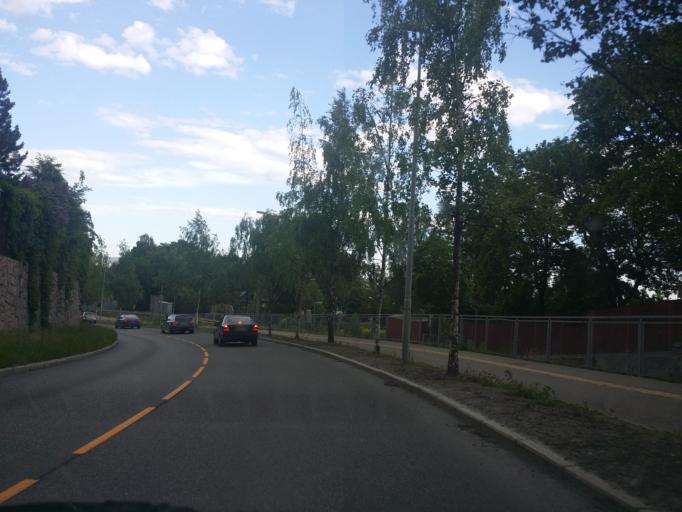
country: NO
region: Oslo
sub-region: Oslo
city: Sjolyststranda
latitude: 59.9400
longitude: 10.6756
